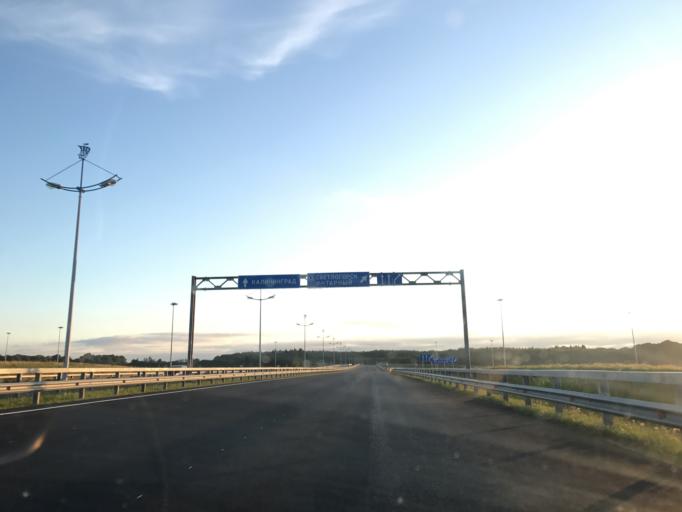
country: RU
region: Kaliningrad
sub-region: Gorod Kaliningrad
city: Pionerskiy
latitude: 54.9085
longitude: 20.2074
